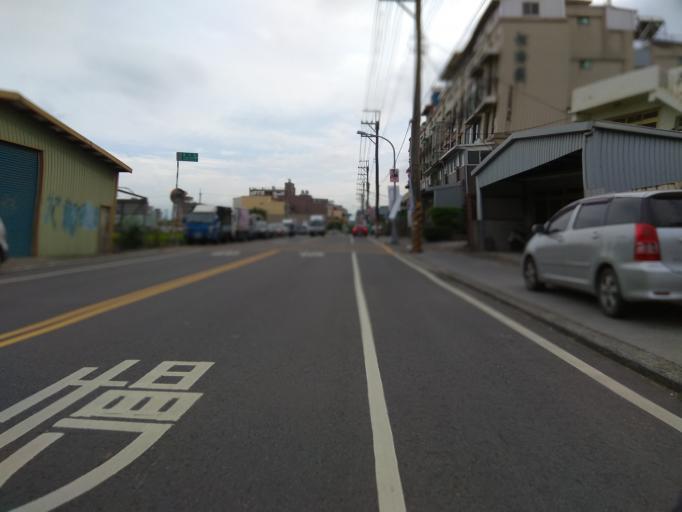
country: TW
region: Taiwan
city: Daxi
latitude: 24.9268
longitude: 121.2060
